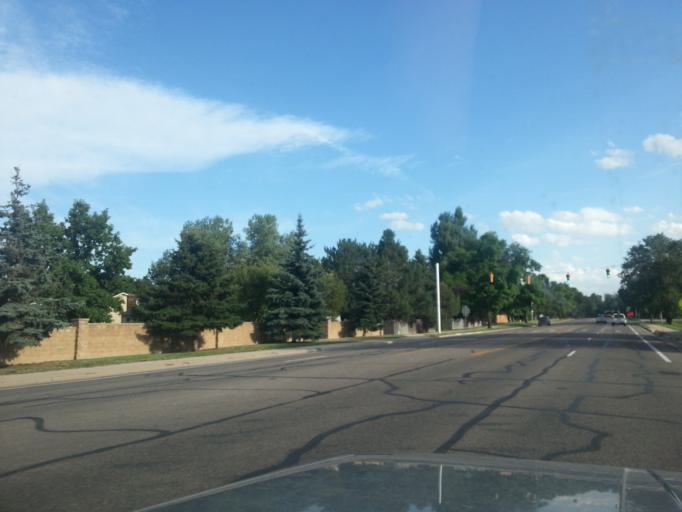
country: US
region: Colorado
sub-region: Larimer County
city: Fort Collins
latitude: 40.5417
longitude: -105.0580
